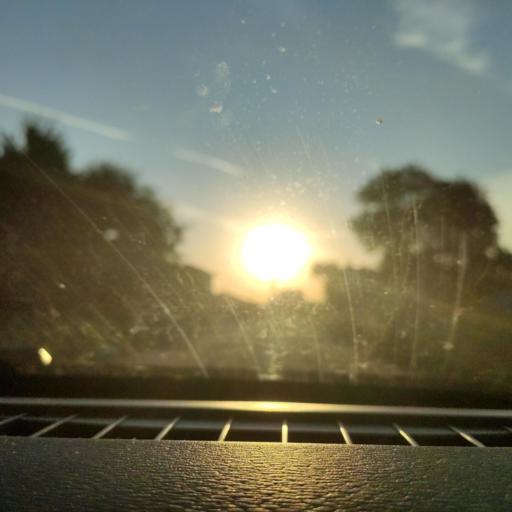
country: RU
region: Voronezj
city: Maslovka
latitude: 51.6141
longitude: 39.2699
